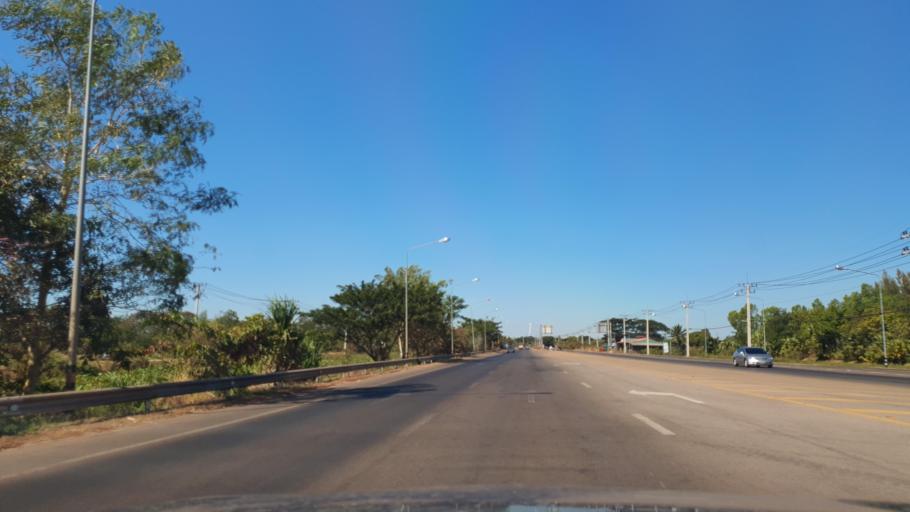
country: TH
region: Sakon Nakhon
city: Sakon Nakhon
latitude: 17.2603
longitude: 104.1555
